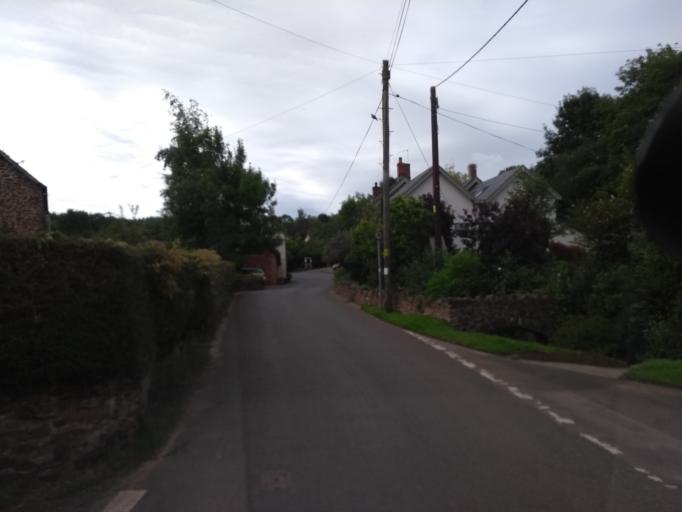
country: GB
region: England
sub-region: Somerset
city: Williton
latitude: 51.1297
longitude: -3.3261
